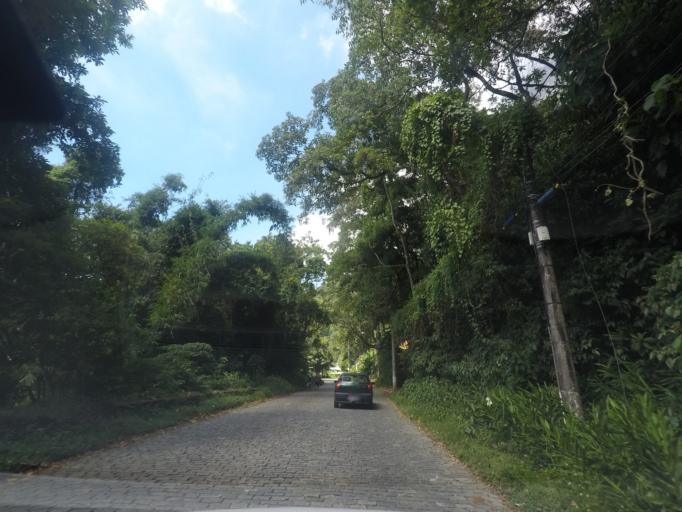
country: BR
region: Rio de Janeiro
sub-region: Petropolis
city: Petropolis
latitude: -22.5424
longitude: -43.1813
